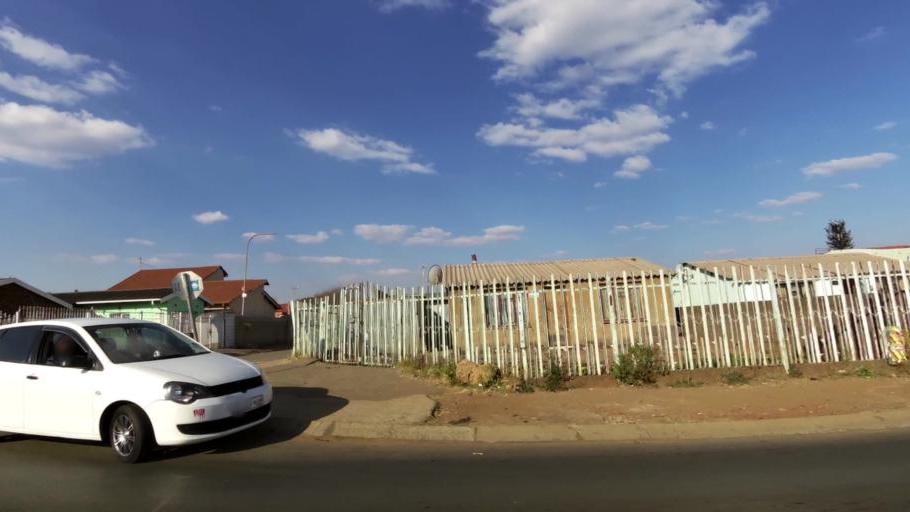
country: ZA
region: Gauteng
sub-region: City of Johannesburg Metropolitan Municipality
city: Roodepoort
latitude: -26.2121
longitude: 27.8766
